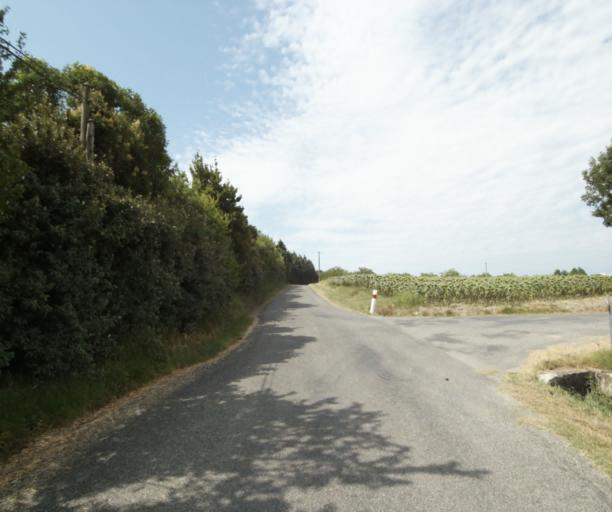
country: FR
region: Midi-Pyrenees
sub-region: Departement de la Haute-Garonne
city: Saint-Felix-Lauragais
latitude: 43.4242
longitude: 1.9148
